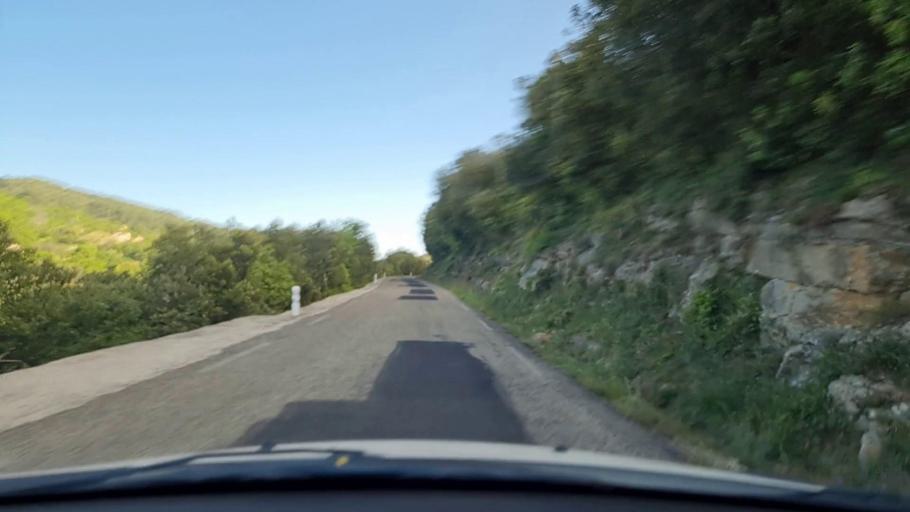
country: FR
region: Languedoc-Roussillon
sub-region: Departement du Gard
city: Les Salles-du-Gardon
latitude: 44.1784
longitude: 4.0209
